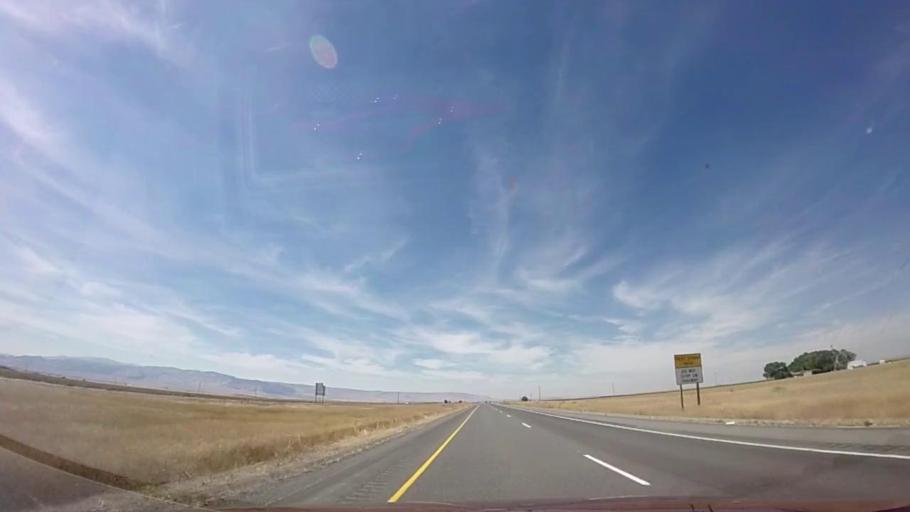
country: US
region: Idaho
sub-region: Minidoka County
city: Rupert
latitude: 42.3397
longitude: -113.2296
